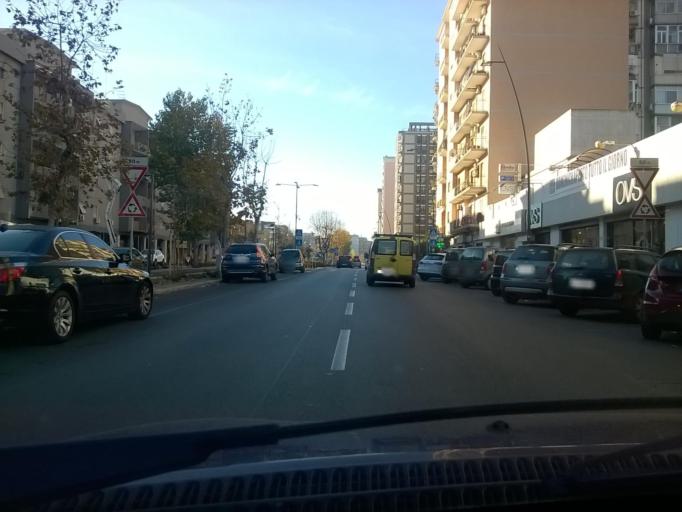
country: IT
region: Apulia
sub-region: Provincia di Taranto
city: Taranto
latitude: 40.4570
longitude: 17.2655
